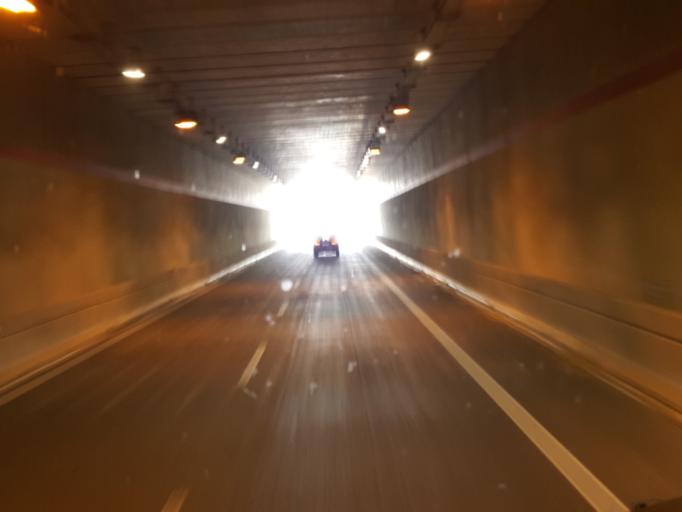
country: IT
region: Apulia
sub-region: Provincia di Bari
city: Palo del Colle
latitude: 41.0478
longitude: 16.7111
